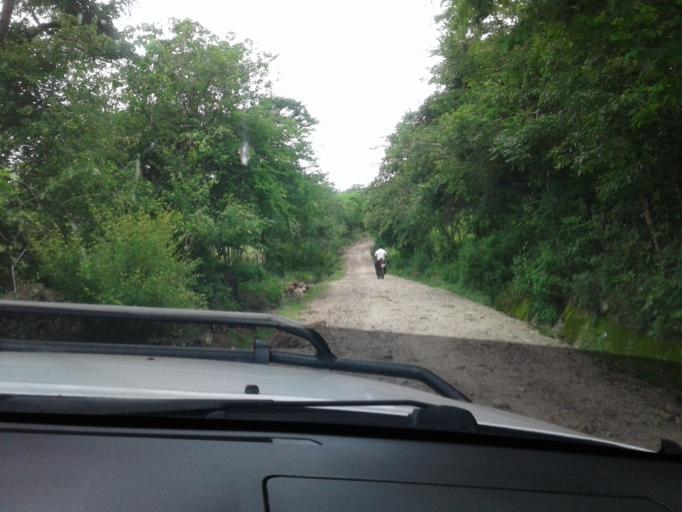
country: NI
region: Leon
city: Santa Rosa del Penon
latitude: 12.9033
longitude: -86.2138
